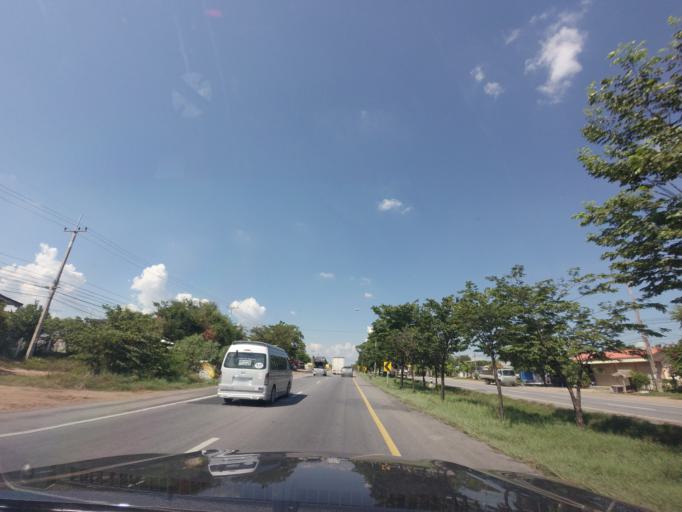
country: TH
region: Nakhon Ratchasima
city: Non Sung
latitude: 15.1667
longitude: 102.3333
